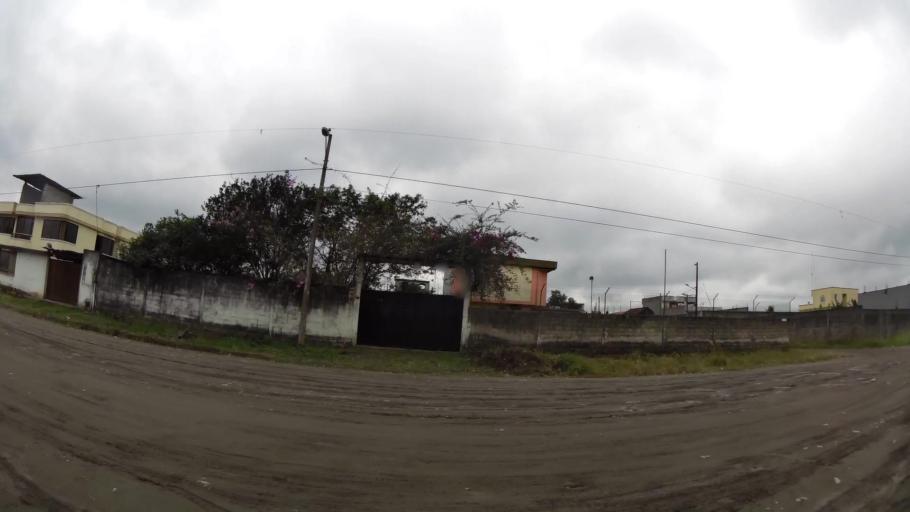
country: EC
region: Santo Domingo de los Tsachilas
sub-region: Canton Santo Domingo de los Colorados
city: Santo Domingo de los Colorados
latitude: -0.2409
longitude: -79.1594
